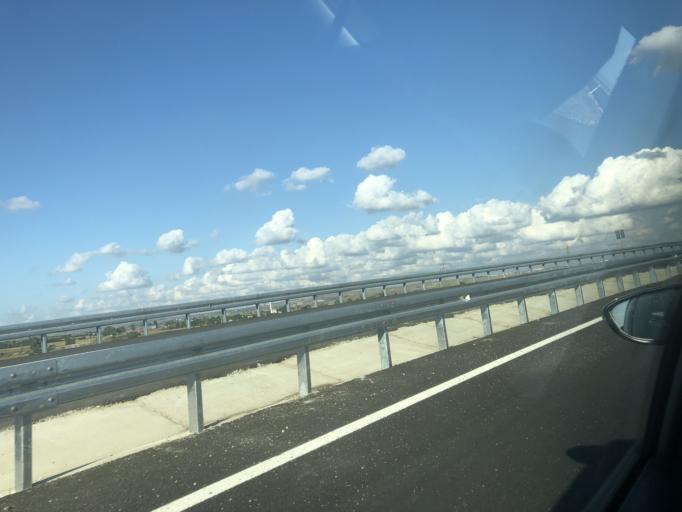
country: TR
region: Istanbul
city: Catalca
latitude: 41.1427
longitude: 28.4795
